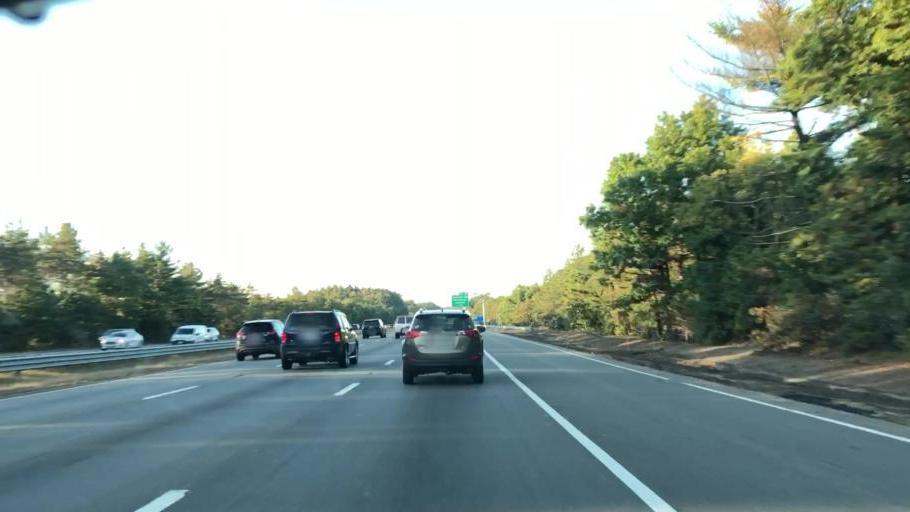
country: US
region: Massachusetts
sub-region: Middlesex County
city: Wilmington
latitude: 42.6067
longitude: -71.1724
